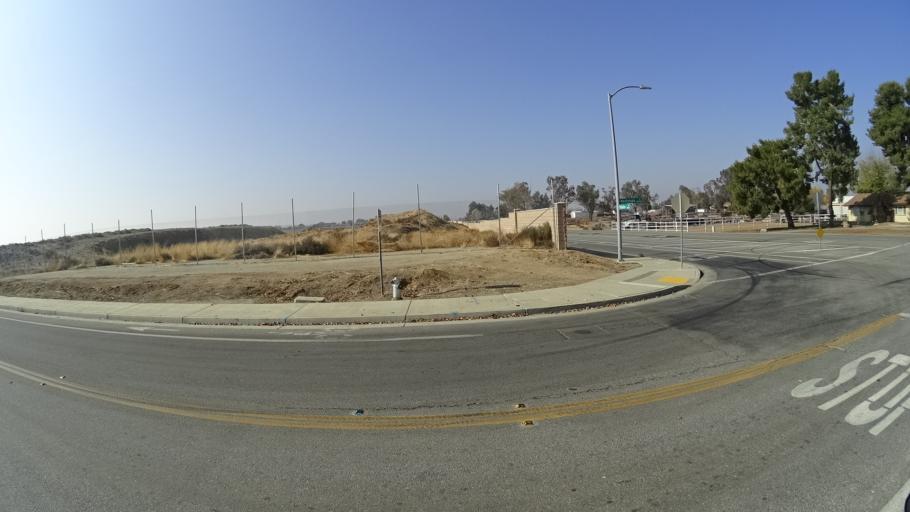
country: US
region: California
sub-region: Kern County
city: Oildale
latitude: 35.4123
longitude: -118.8787
